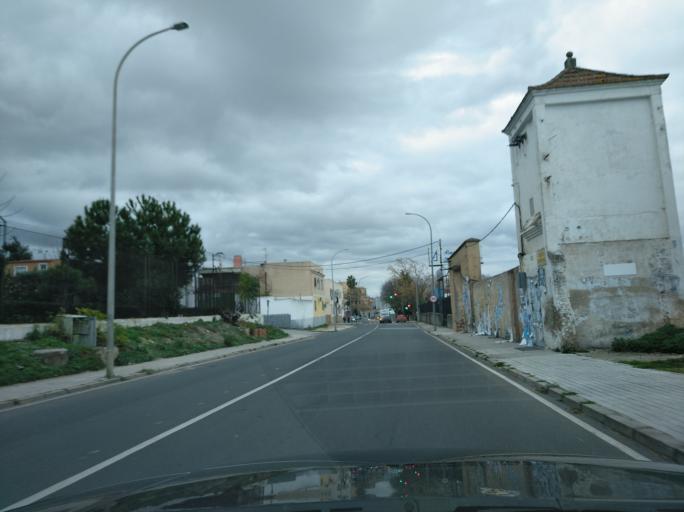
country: ES
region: Extremadura
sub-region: Provincia de Badajoz
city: Badajoz
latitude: 38.8942
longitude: -6.9825
